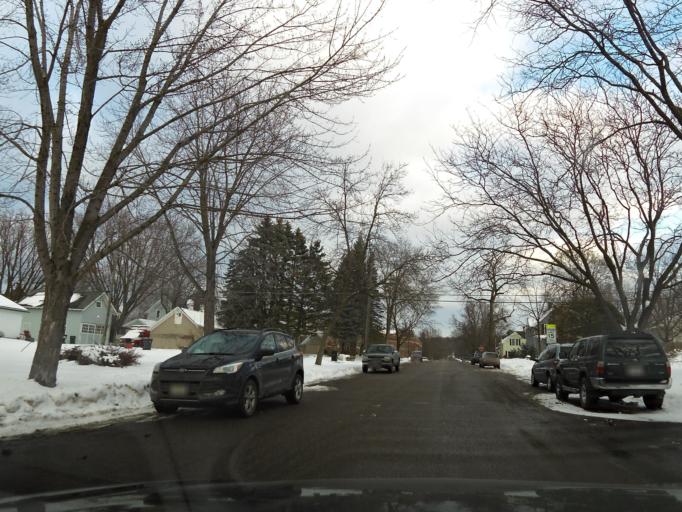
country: US
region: Wisconsin
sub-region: Saint Croix County
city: Hudson
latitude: 44.9815
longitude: -92.7555
